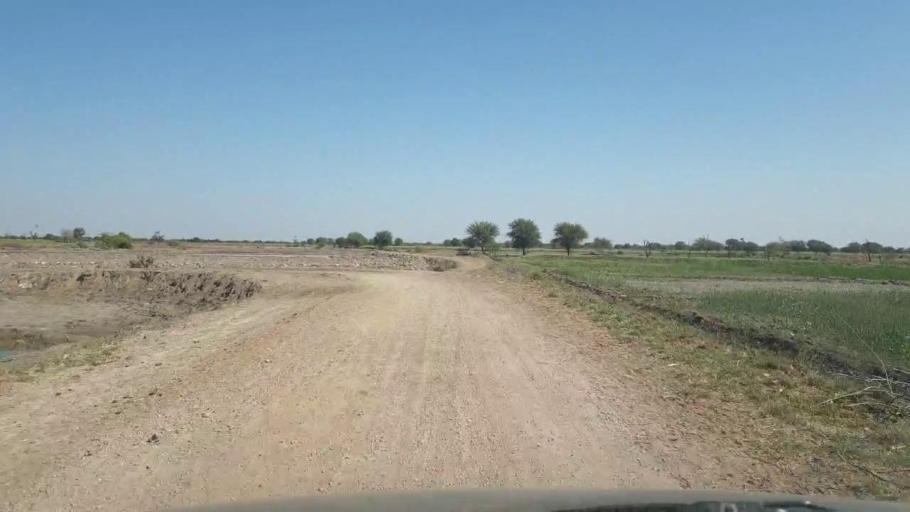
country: PK
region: Sindh
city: Dhoro Naro
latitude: 25.4120
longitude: 69.6239
